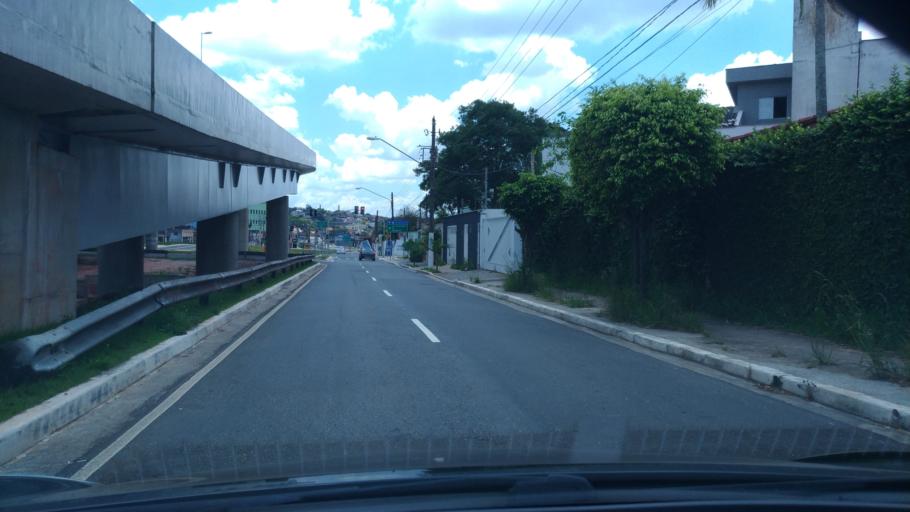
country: BR
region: Sao Paulo
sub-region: Sao Bernardo Do Campo
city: Sao Bernardo do Campo
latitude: -23.7100
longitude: -46.5874
